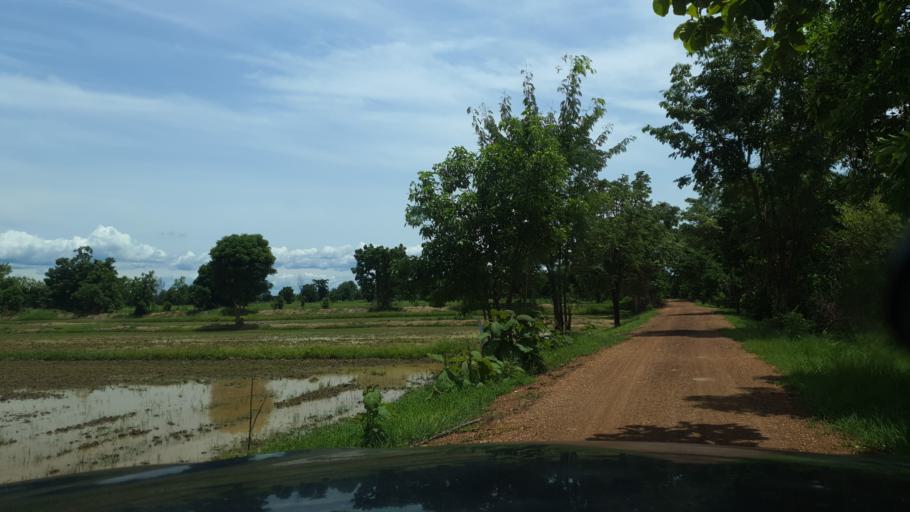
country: TH
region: Sukhothai
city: Ban Na
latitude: 17.0705
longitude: 99.6971
